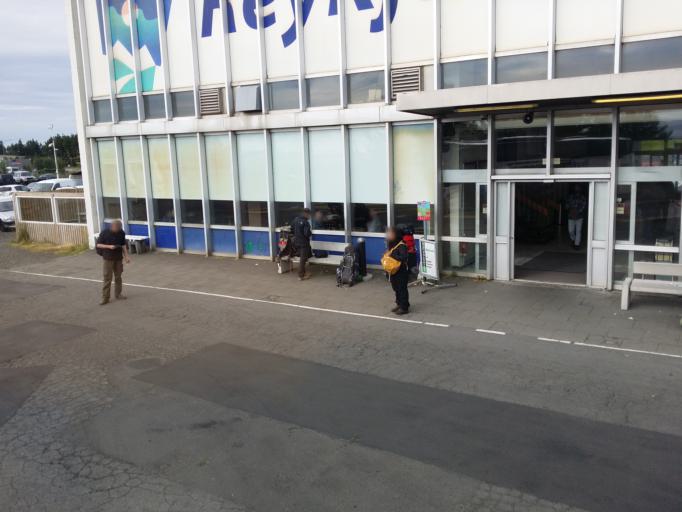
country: IS
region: Capital Region
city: Kopavogur
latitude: 64.1373
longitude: -21.9348
